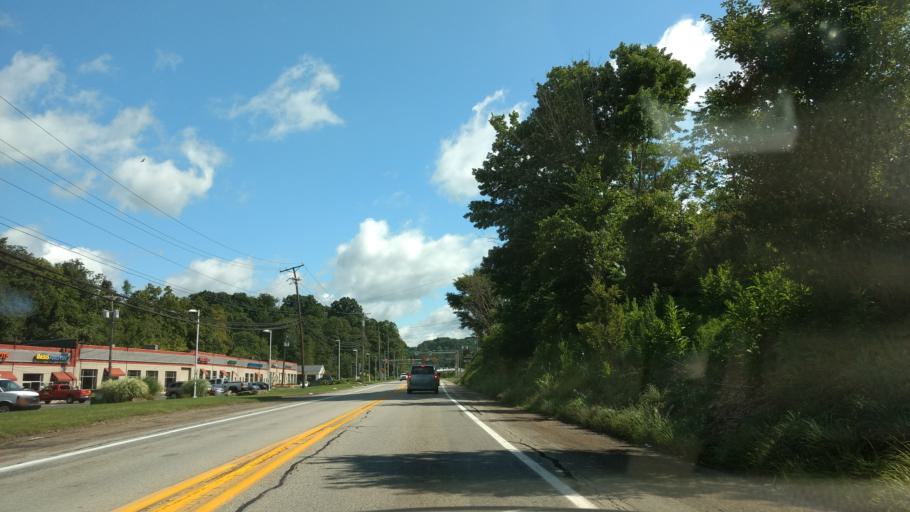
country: US
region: Pennsylvania
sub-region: Westmoreland County
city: Murrysville
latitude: 40.4564
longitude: -79.7097
